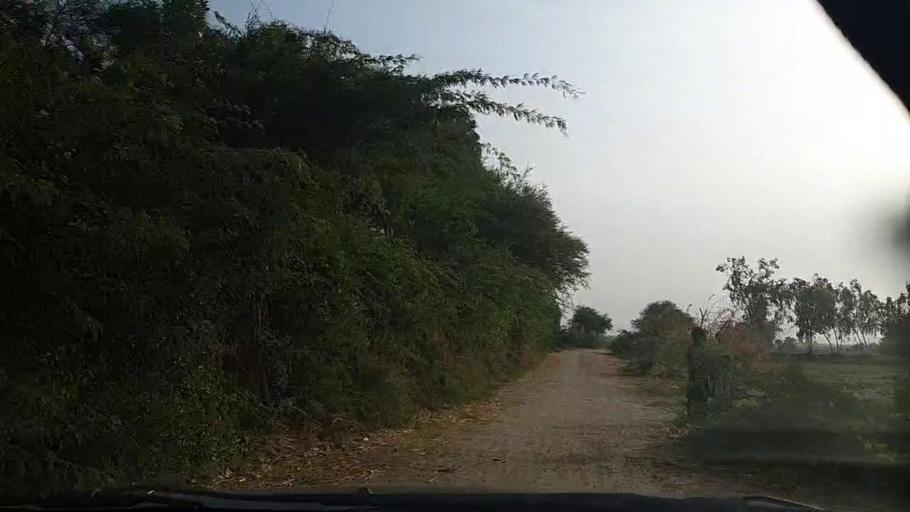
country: PK
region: Sindh
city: Thatta
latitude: 24.7311
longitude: 67.9155
